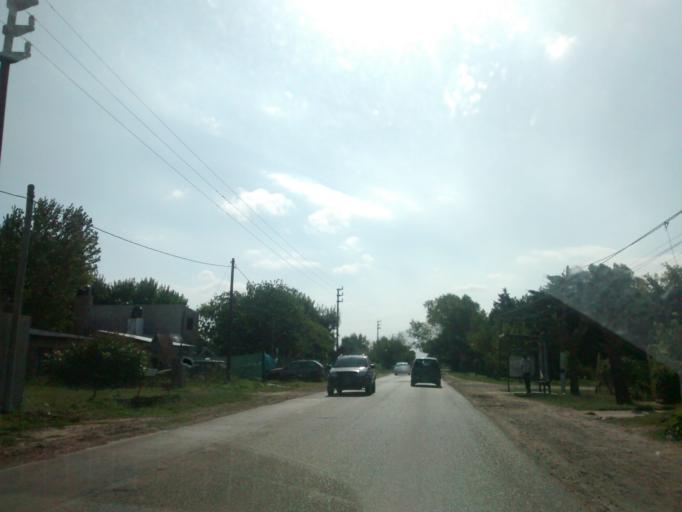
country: AR
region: Buenos Aires
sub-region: Partido de La Plata
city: La Plata
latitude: -34.9731
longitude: -57.8722
